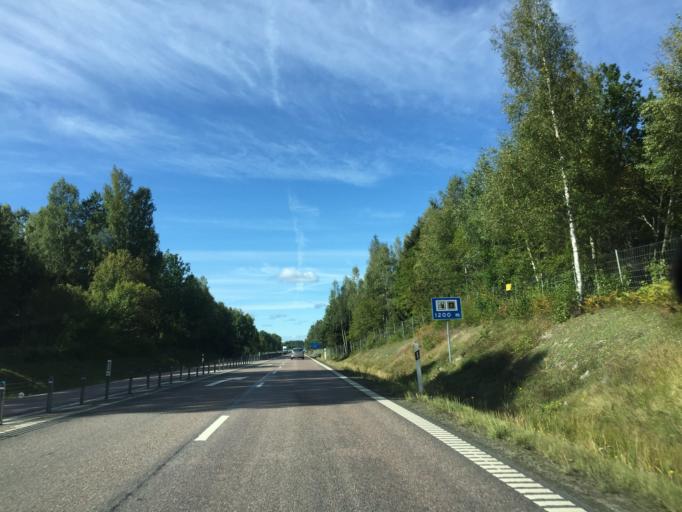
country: SE
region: Vaestmanland
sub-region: Hallstahammars Kommun
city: Kolback
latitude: 59.5859
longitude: 16.2754
